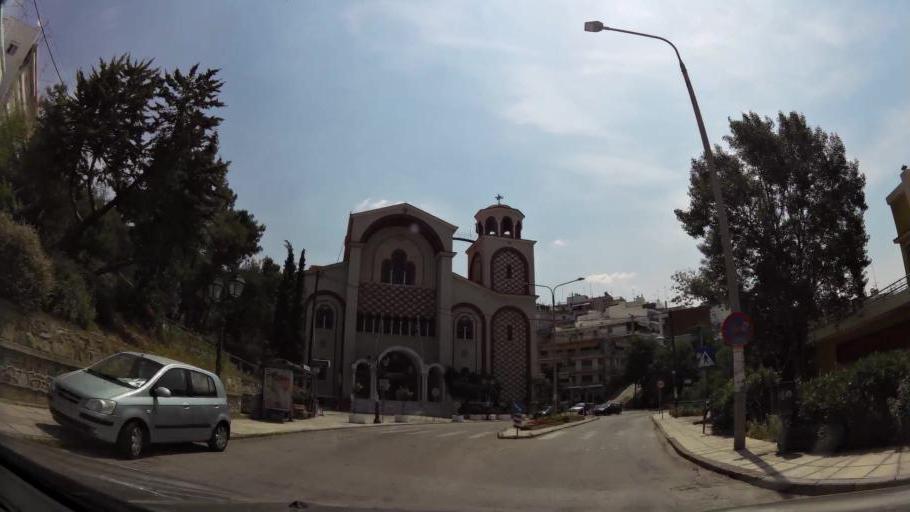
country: GR
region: Central Macedonia
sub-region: Nomos Thessalonikis
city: Agios Pavlos
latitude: 40.6314
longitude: 22.9662
